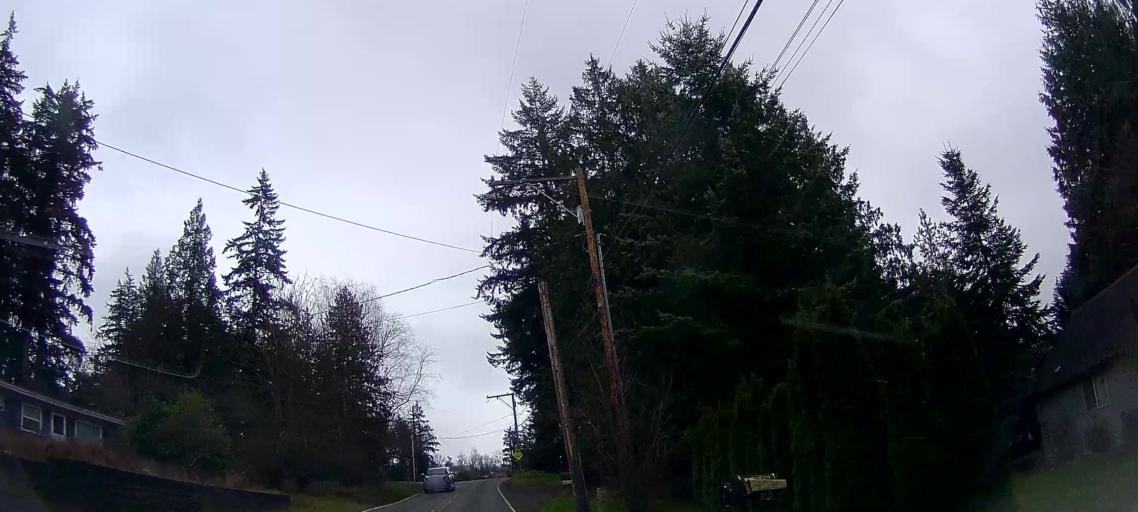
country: US
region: Washington
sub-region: Skagit County
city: Mount Vernon
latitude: 48.3976
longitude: -122.3229
